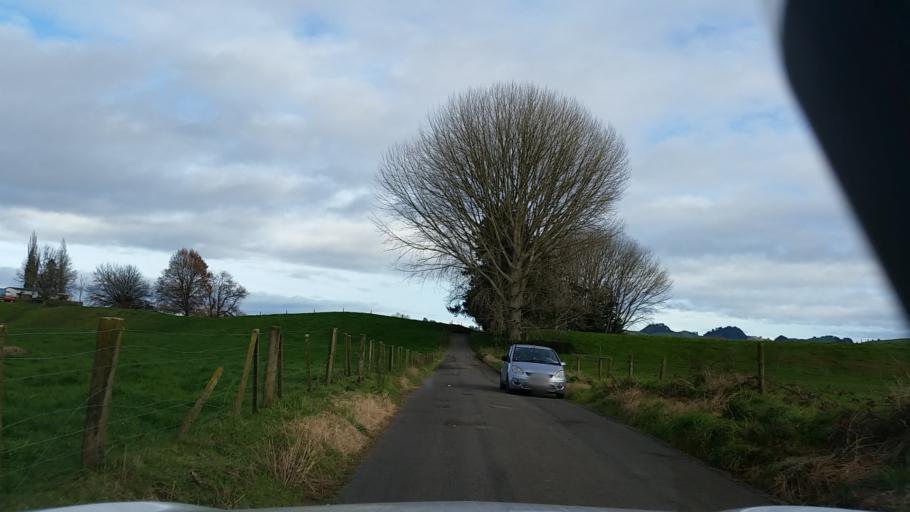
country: NZ
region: Bay of Plenty
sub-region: Rotorua District
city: Rotorua
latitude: -38.4530
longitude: 176.3422
